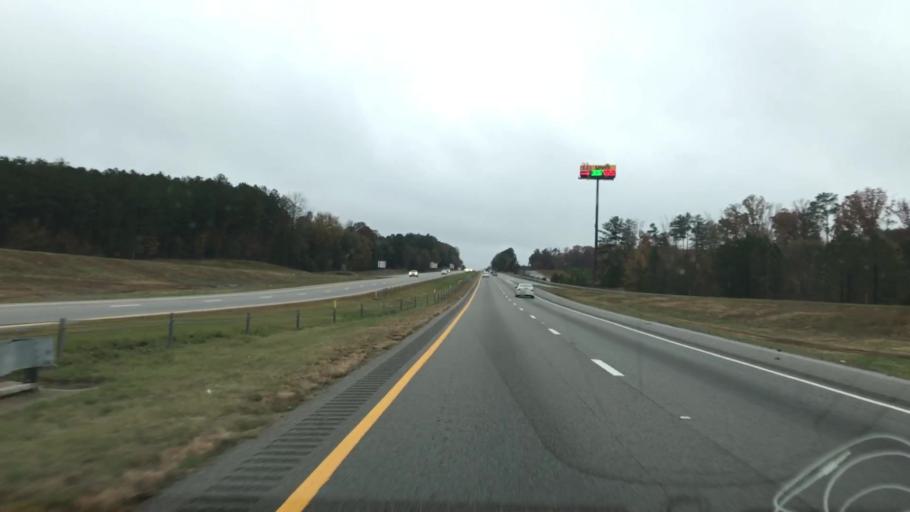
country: US
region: South Carolina
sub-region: Newberry County
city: Newberry
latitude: 34.2939
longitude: -81.5467
